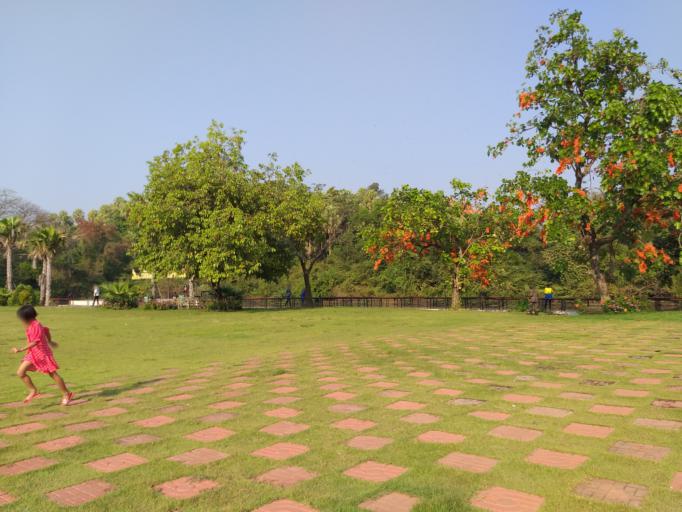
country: TH
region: Changwat Udon Thani
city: Ban Dung
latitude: 17.7427
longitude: 103.3598
